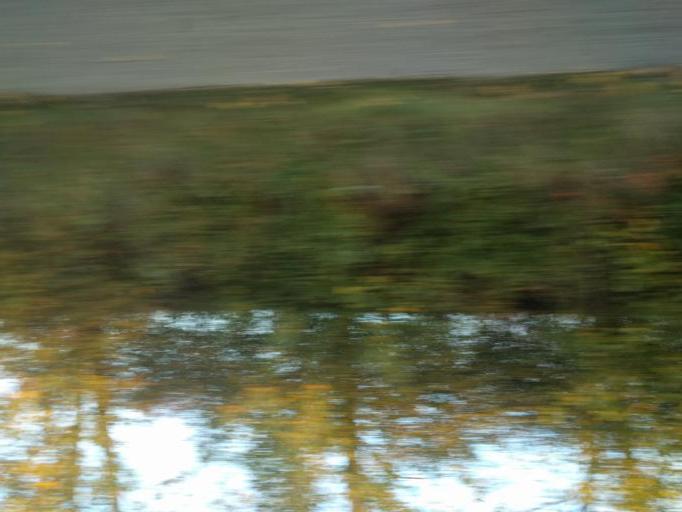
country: DK
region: South Denmark
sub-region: Nyborg Kommune
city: Ullerslev
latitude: 55.3494
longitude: 10.6300
